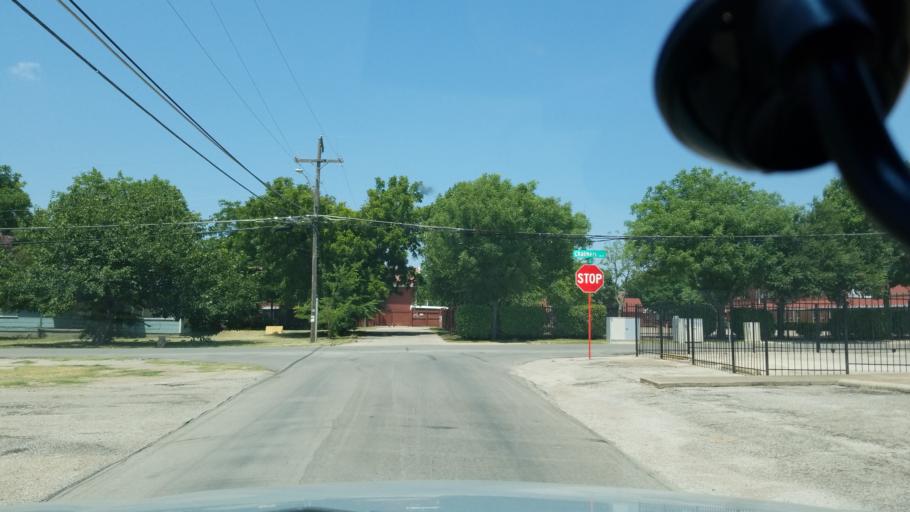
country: US
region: Texas
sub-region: Dallas County
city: Cockrell Hill
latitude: 32.7194
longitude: -96.8621
